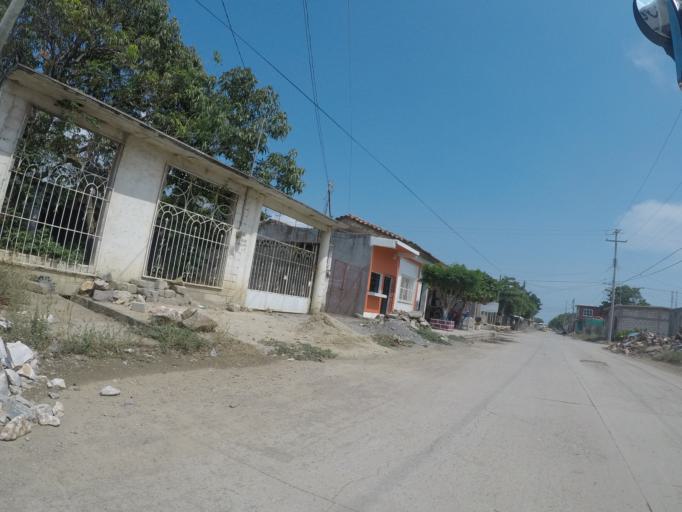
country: MX
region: Oaxaca
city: Union Hidalgo
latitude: 16.4732
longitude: -94.8355
